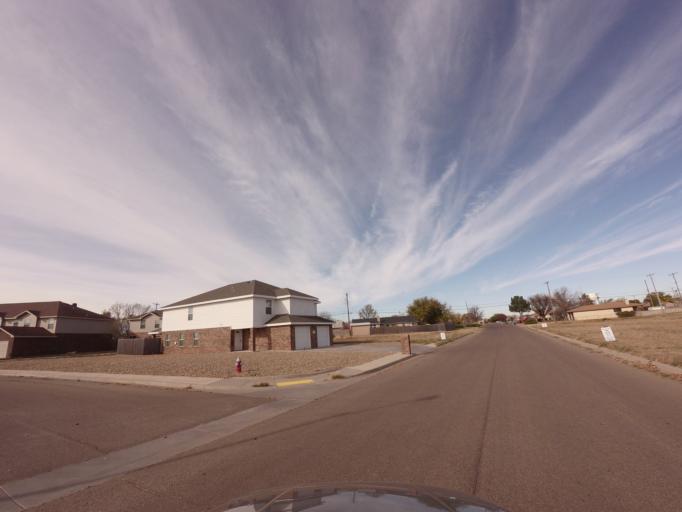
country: US
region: New Mexico
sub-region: Curry County
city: Clovis
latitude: 34.4226
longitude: -103.2223
